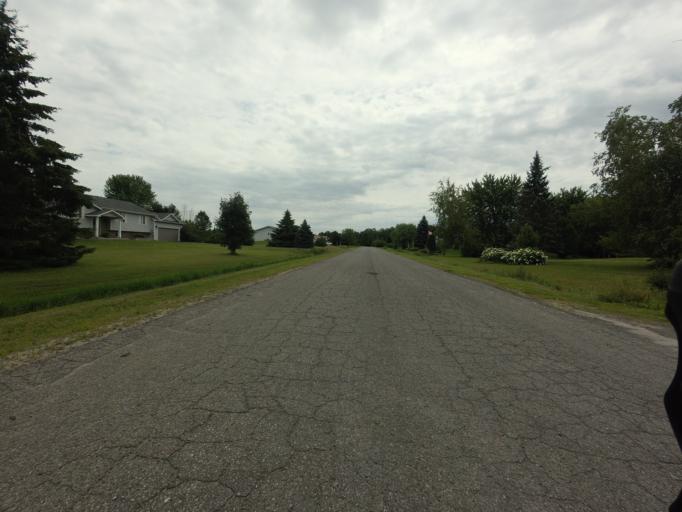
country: CA
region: Ontario
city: Bells Corners
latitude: 45.0242
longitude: -75.6933
